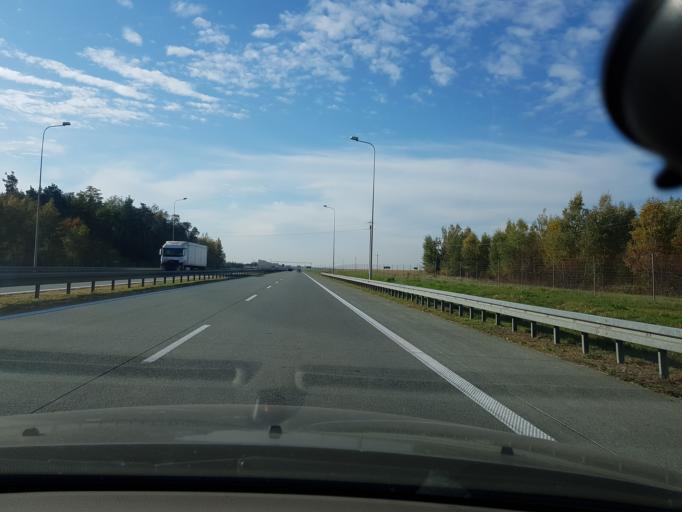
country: PL
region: Lodz Voivodeship
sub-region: Powiat skierniewicki
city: Kowiesy
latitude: 51.8597
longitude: 20.3787
